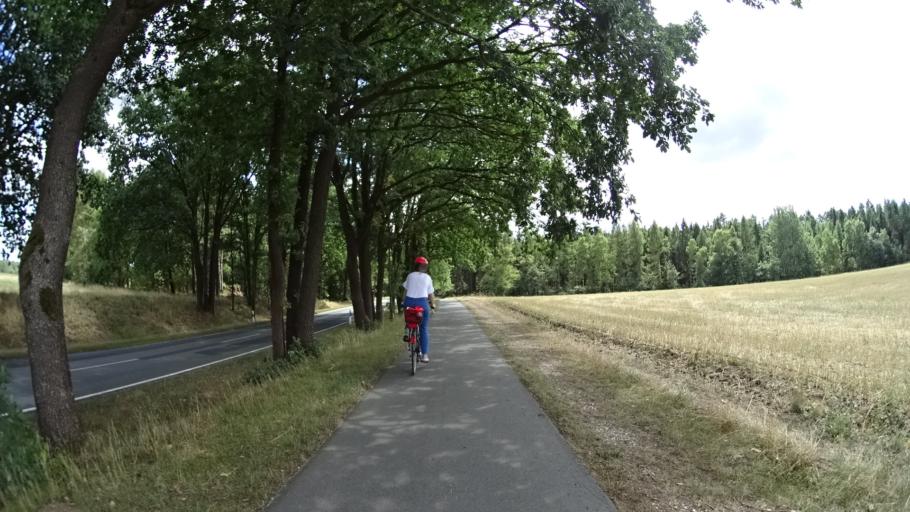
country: DE
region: Lower Saxony
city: Undeloh
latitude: 53.2061
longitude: 9.9583
